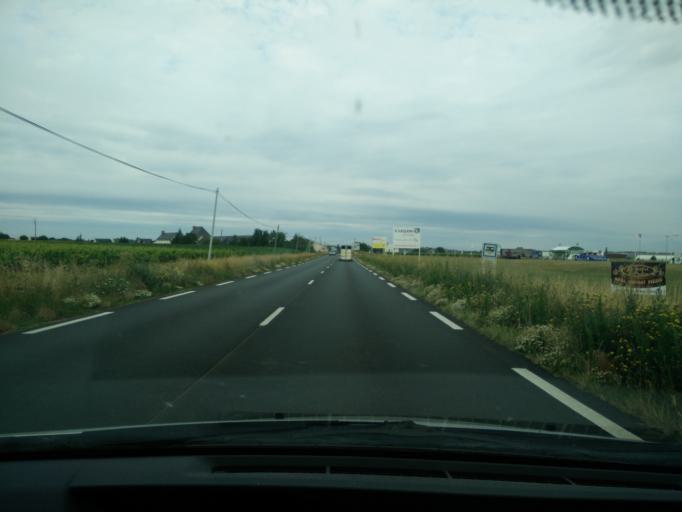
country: FR
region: Pays de la Loire
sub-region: Departement de Maine-et-Loire
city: Brissac-Quince
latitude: 47.3398
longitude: -0.4324
